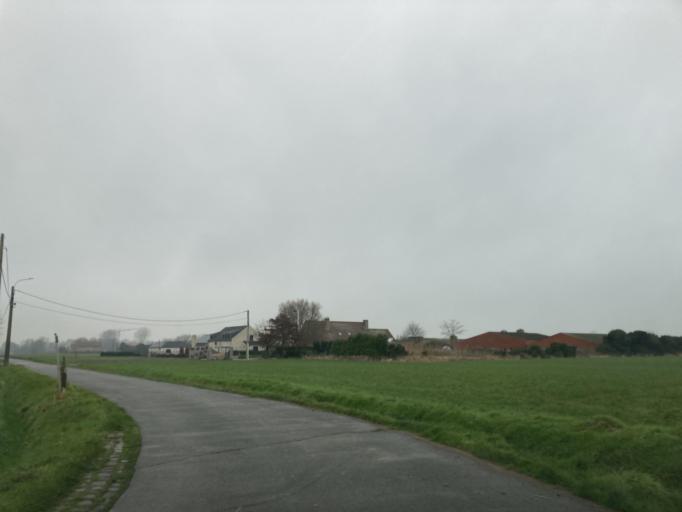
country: BE
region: Flanders
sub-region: Provincie West-Vlaanderen
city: Ichtegem
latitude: 51.1306
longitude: 3.0521
